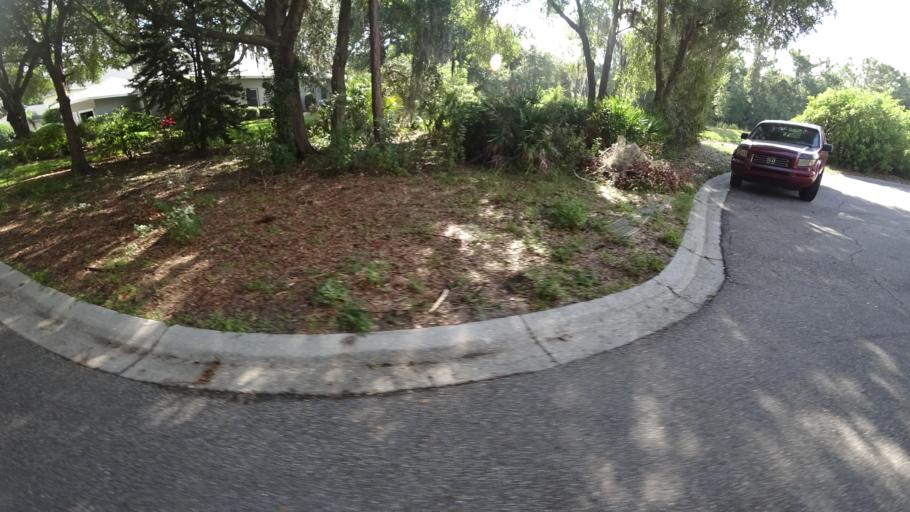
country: US
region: Florida
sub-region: Sarasota County
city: The Meadows
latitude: 27.4260
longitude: -82.4332
